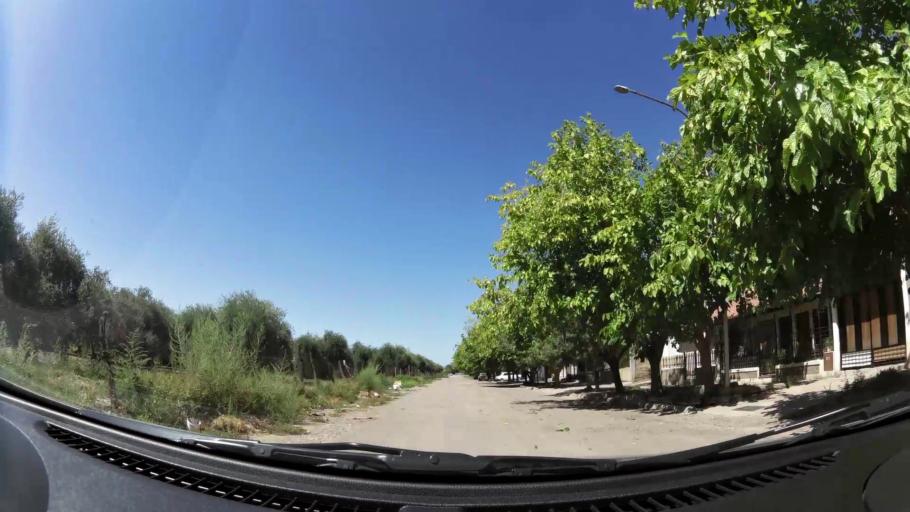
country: AR
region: Mendoza
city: Villa Nueva
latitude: -32.8780
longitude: -68.7925
